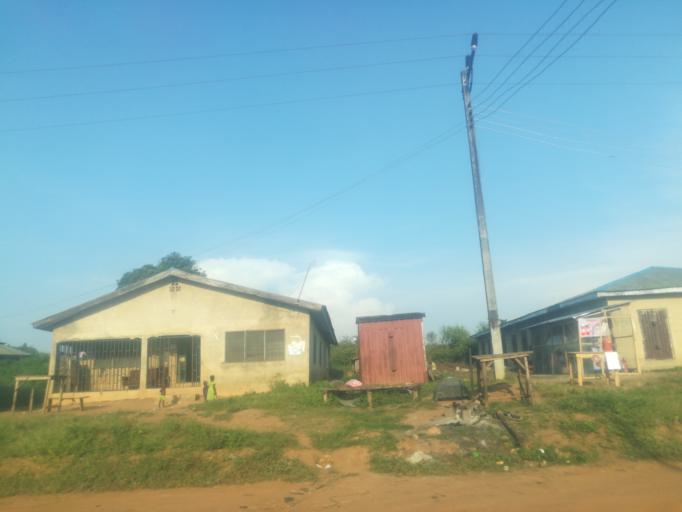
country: NG
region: Oyo
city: Moniya
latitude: 7.5529
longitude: 3.8902
